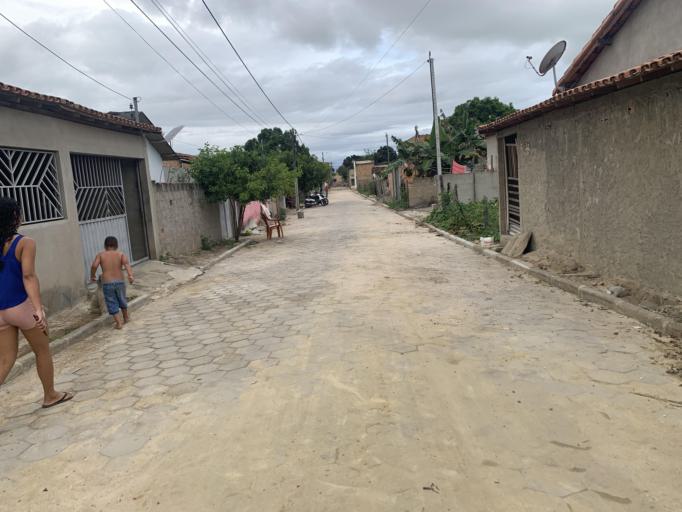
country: BR
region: Bahia
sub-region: Medeiros Neto
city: Medeiros Neto
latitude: -17.3911
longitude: -40.2325
